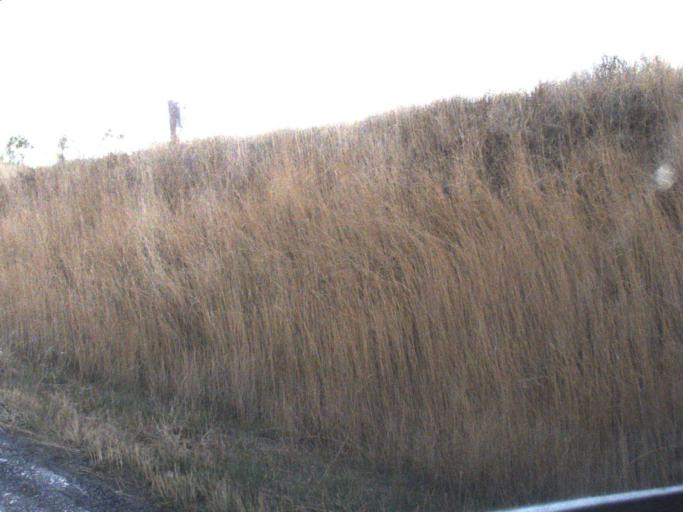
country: US
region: Washington
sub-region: Stevens County
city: Kettle Falls
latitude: 48.4760
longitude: -118.1692
